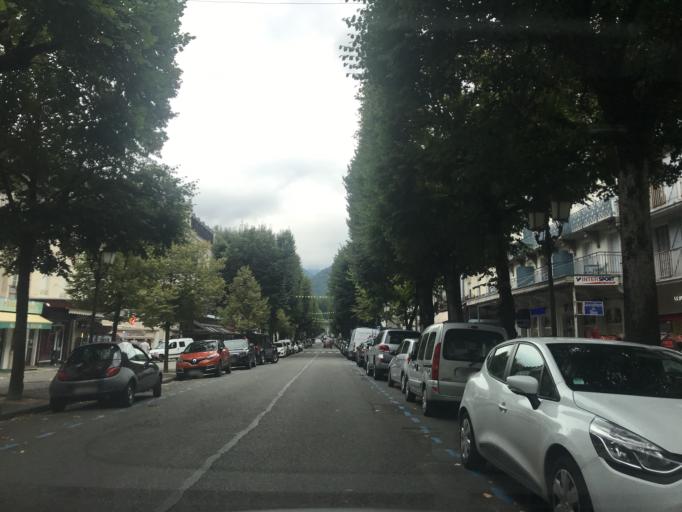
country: FR
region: Midi-Pyrenees
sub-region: Departement de la Haute-Garonne
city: Bagneres-de-Luchon
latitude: 42.7903
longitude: 0.5915
